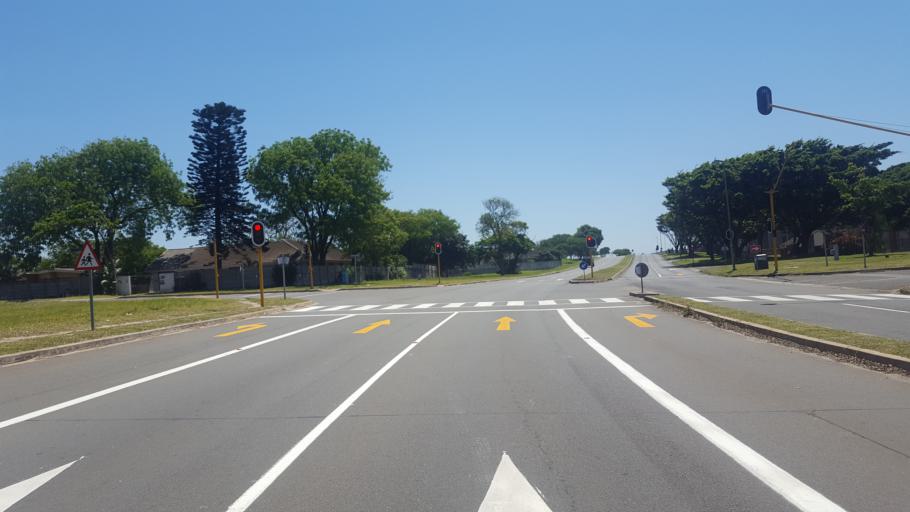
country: ZA
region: KwaZulu-Natal
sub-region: uThungulu District Municipality
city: Richards Bay
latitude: -28.7619
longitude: 32.0558
